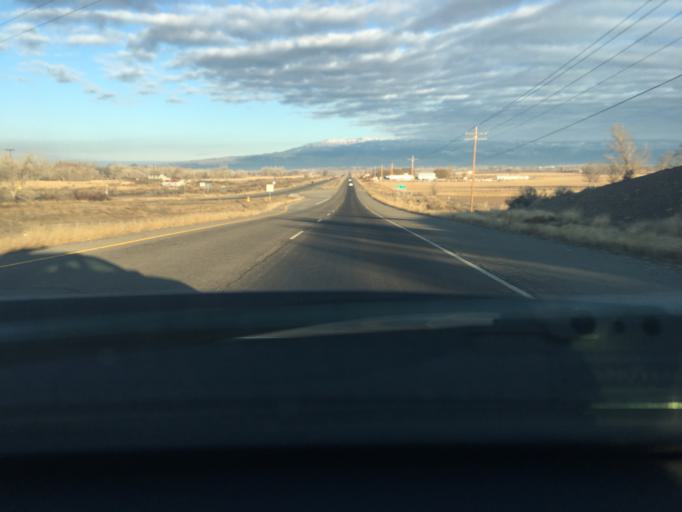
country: US
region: Colorado
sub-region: Montrose County
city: Olathe
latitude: 38.6672
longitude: -107.9980
